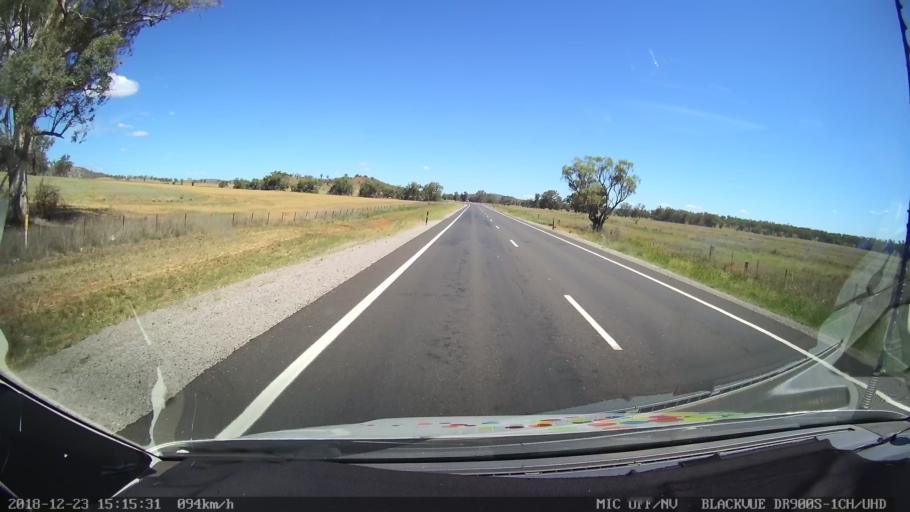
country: AU
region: New South Wales
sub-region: Tamworth Municipality
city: Manilla
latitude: -30.7868
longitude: 150.7431
